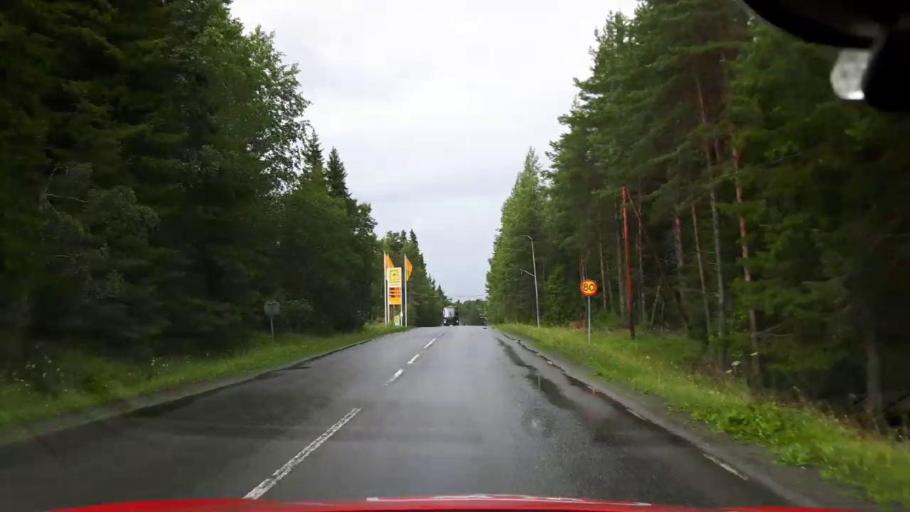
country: SE
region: Jaemtland
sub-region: Krokoms Kommun
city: Krokom
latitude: 63.3424
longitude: 14.2671
